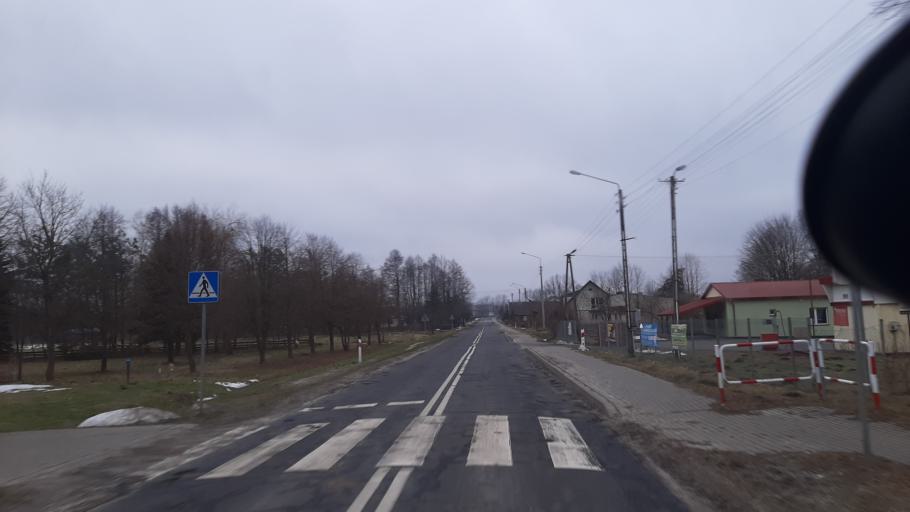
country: PL
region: Lublin Voivodeship
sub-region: Powiat wlodawski
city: Hansk
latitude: 51.5626
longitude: 23.3794
